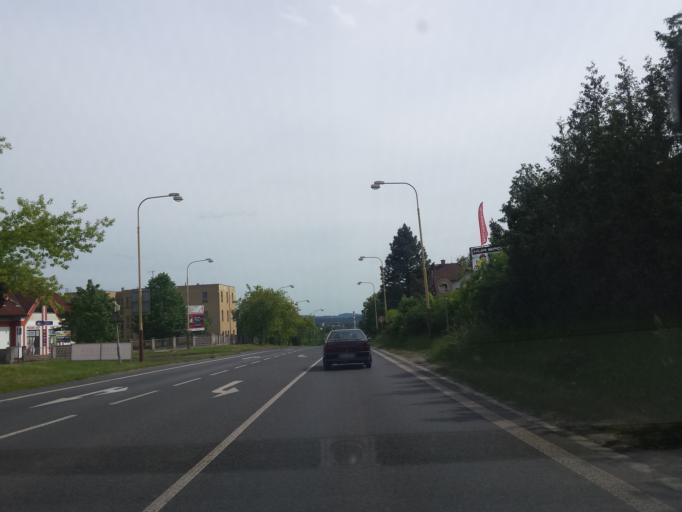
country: CZ
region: Liberecky
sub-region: Okres Ceska Lipa
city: Ceska Lipa
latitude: 50.6927
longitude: 14.5414
